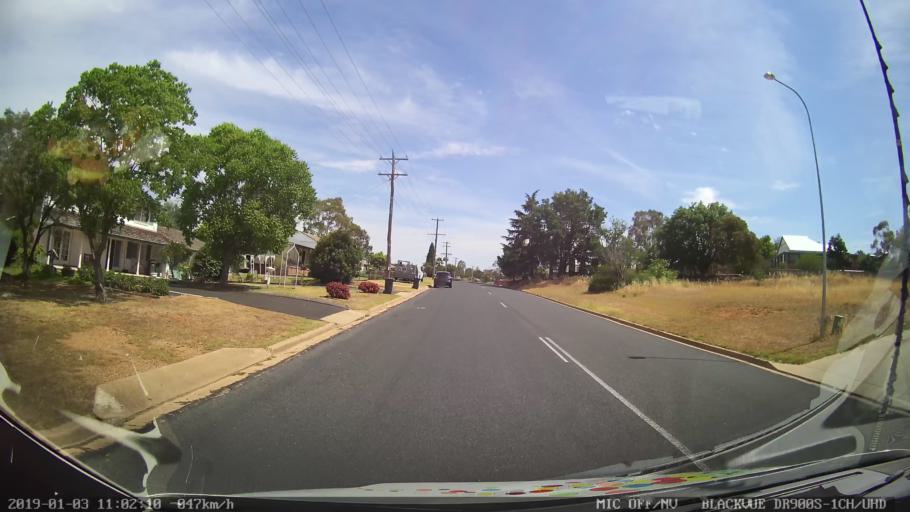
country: AU
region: New South Wales
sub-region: Young
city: Young
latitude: -34.2998
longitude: 148.2991
